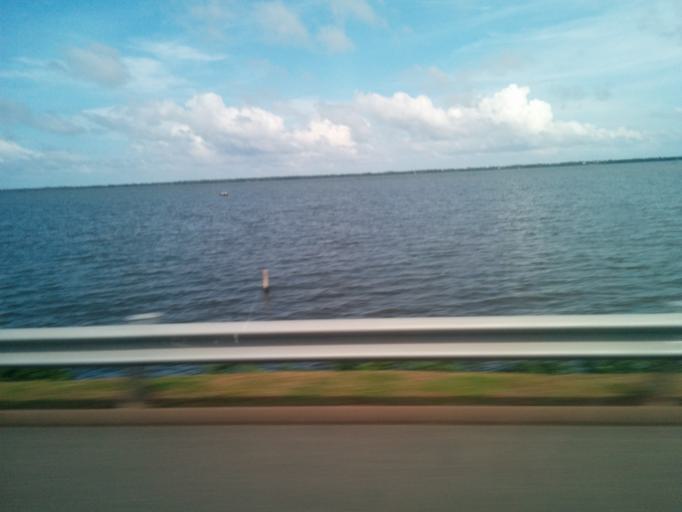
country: LK
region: Western
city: Katunayaka
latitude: 7.1387
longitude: 79.8682
